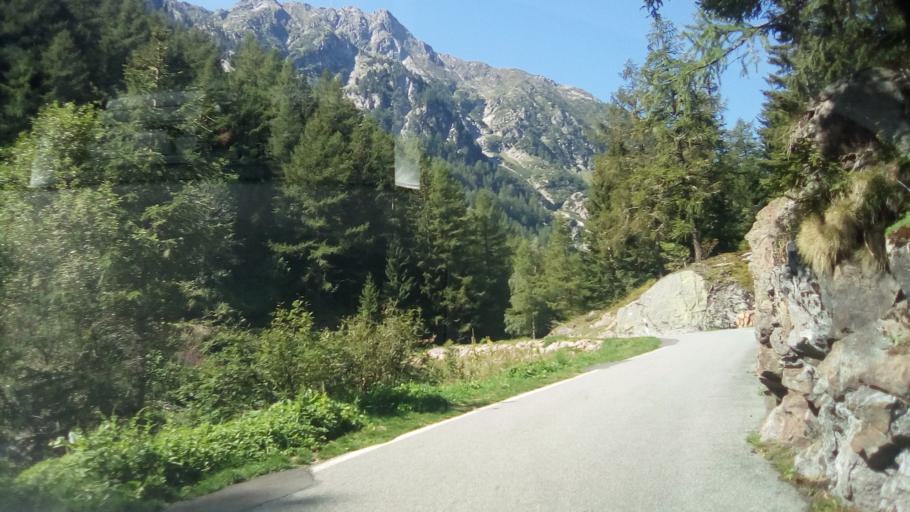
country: CH
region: Valais
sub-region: Saint-Maurice District
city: Salvan
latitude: 46.1393
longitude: 7.0056
